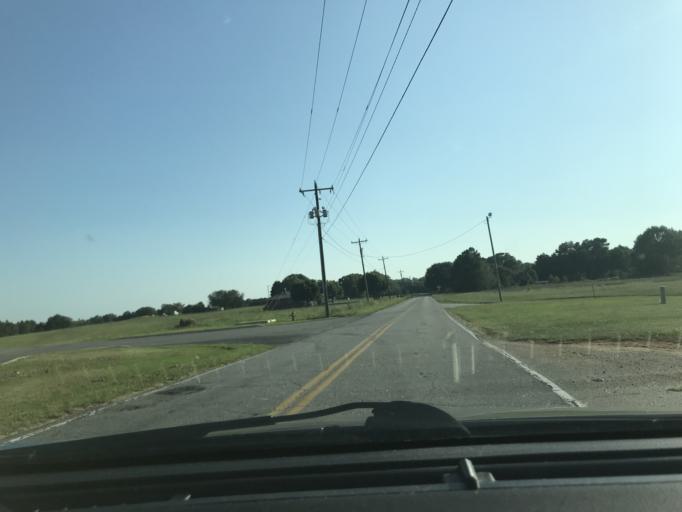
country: US
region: South Carolina
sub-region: Cherokee County
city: Gaffney
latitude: 35.1459
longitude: -81.7466
